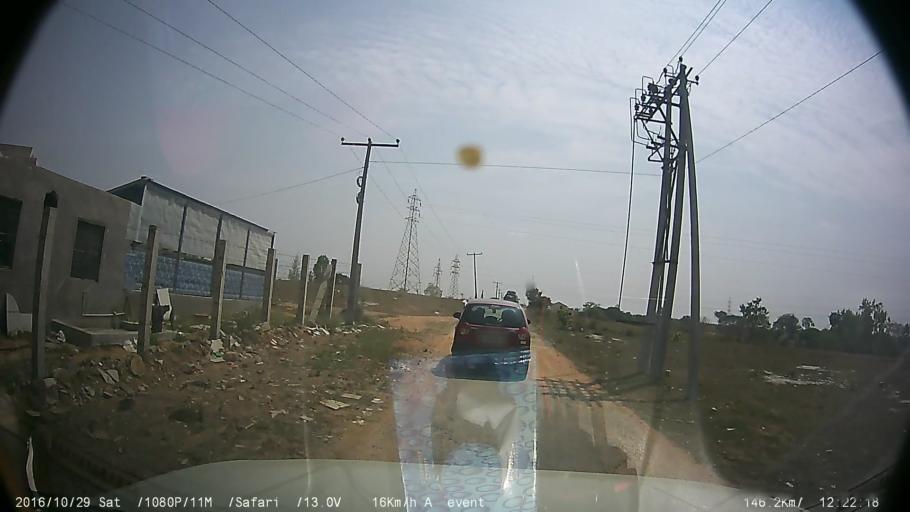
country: IN
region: Karnataka
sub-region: Mysore
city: Mysore
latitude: 12.3639
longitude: 76.5599
